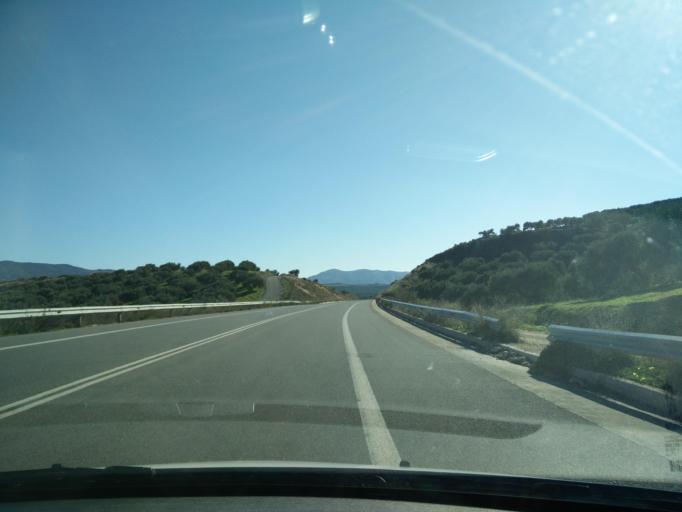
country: GR
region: Crete
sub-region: Nomos Irakleiou
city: Arkalochori
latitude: 35.1136
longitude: 25.2904
